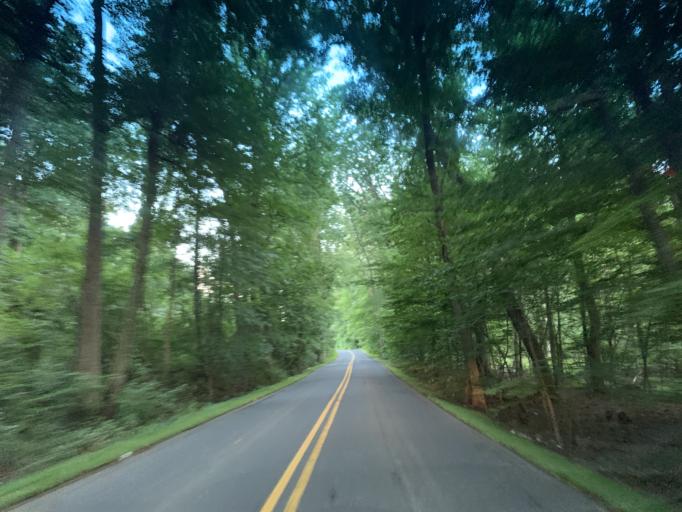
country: US
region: Maryland
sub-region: Harford County
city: Aberdeen
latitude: 39.5338
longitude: -76.1490
